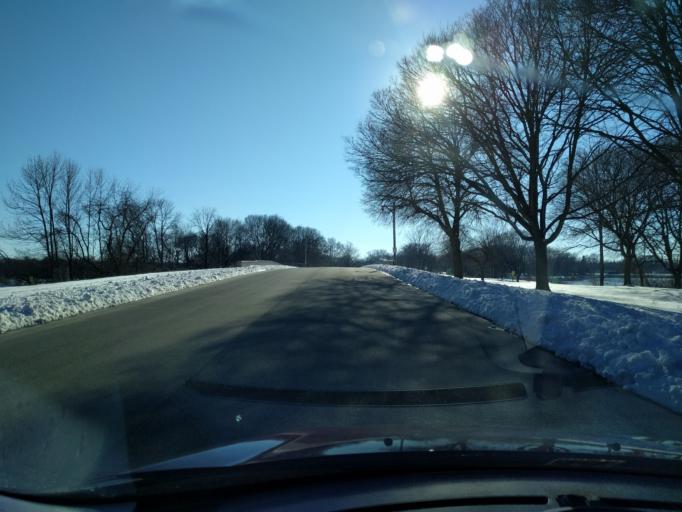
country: US
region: Wisconsin
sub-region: Milwaukee County
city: Whitefish Bay
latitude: 43.1115
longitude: -87.9256
